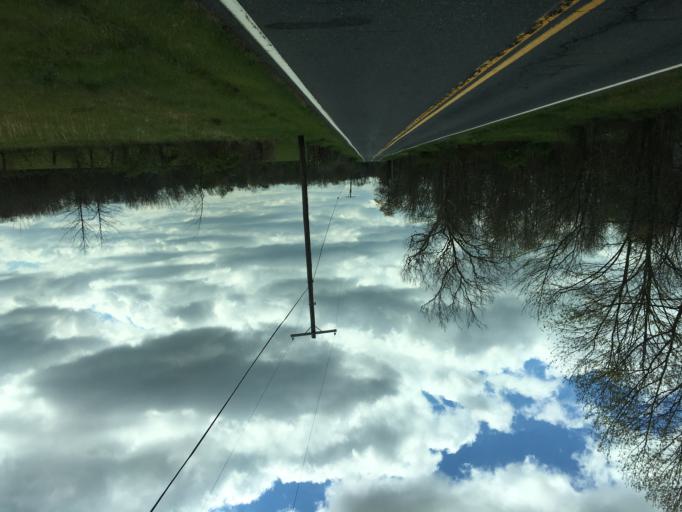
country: US
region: Maryland
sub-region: Frederick County
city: Thurmont
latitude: 39.5843
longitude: -77.3932
